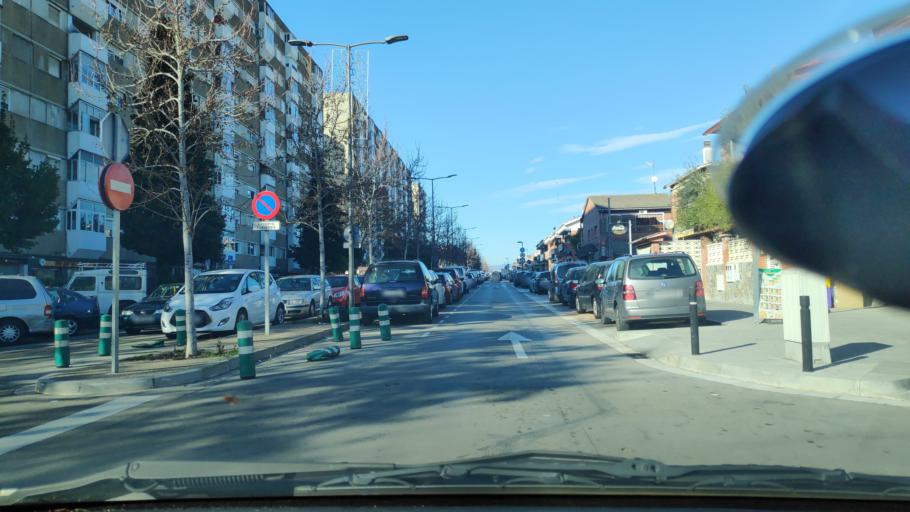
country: ES
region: Catalonia
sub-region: Provincia de Barcelona
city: Barbera del Valles
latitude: 41.5098
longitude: 2.1171
